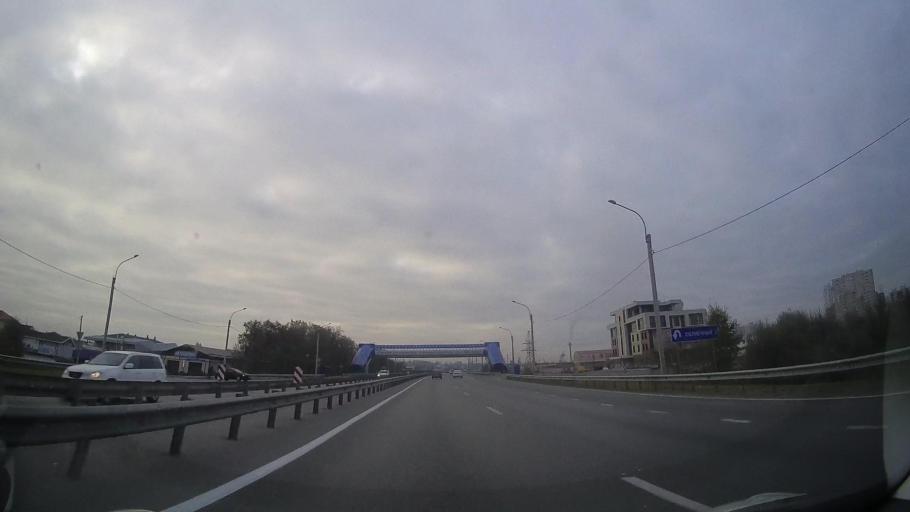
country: RU
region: Rostov
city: Bataysk
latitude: 47.1404
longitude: 39.7761
